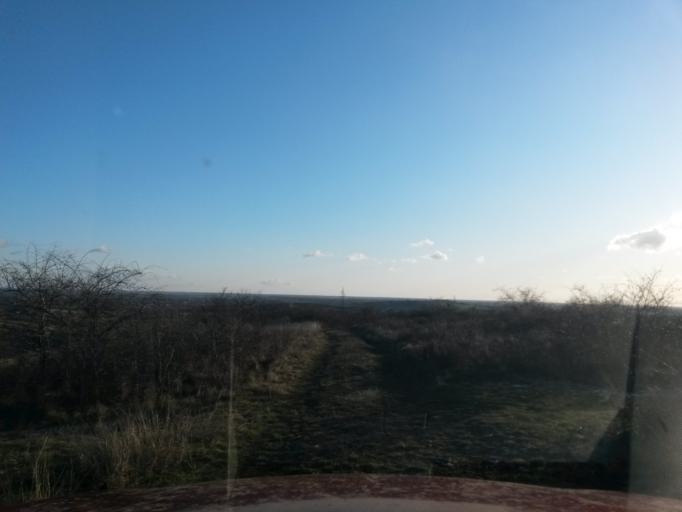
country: HU
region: Borsod-Abauj-Zemplen
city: Sarospatak
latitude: 48.3274
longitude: 21.5380
